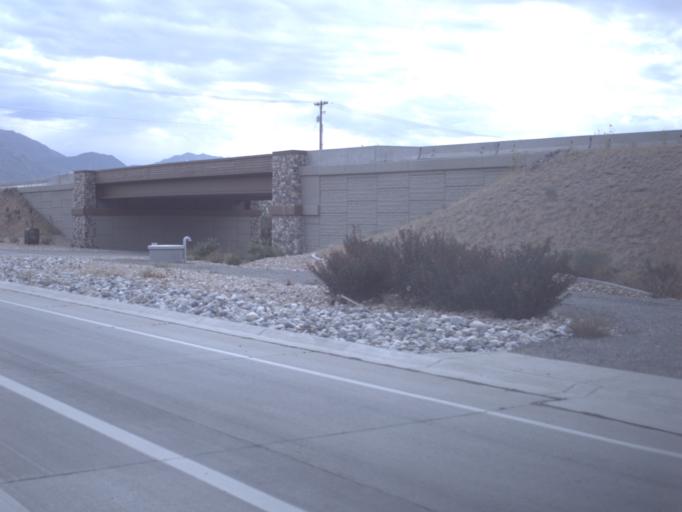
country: US
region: Utah
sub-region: Utah County
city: Lehi
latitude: 40.4328
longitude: -111.8506
